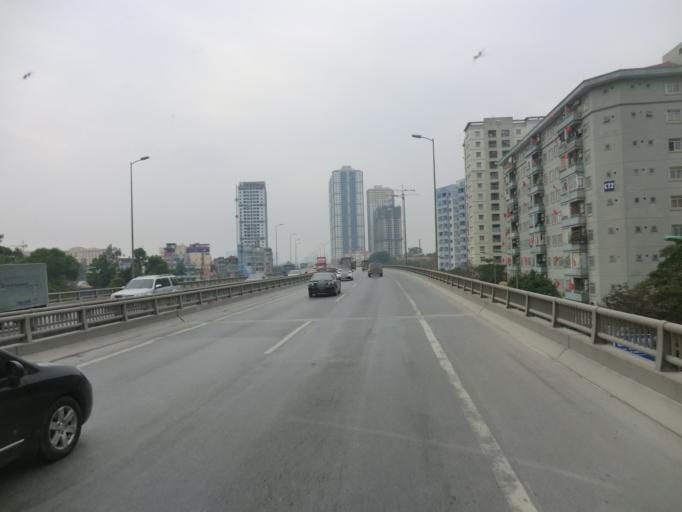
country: VN
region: Ha Noi
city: Van Dien
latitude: 20.9699
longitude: 105.8273
